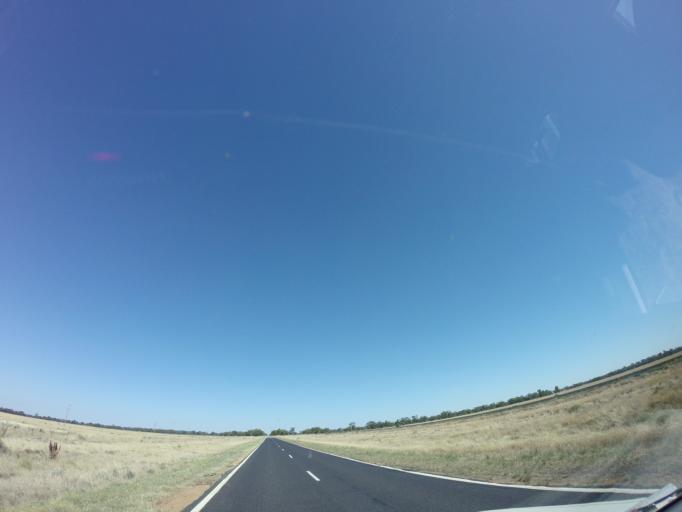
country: AU
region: New South Wales
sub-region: Bogan
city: Nyngan
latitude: -31.7590
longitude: 147.5684
